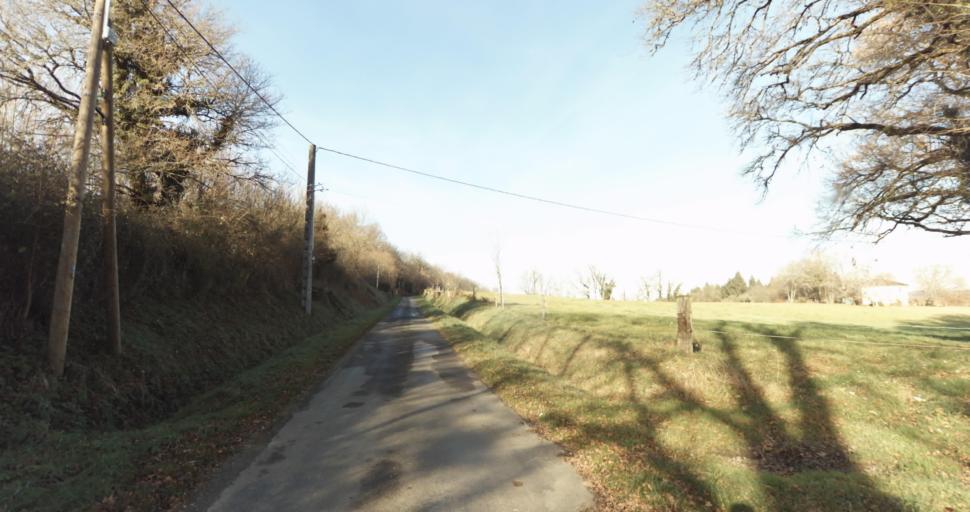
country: FR
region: Limousin
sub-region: Departement de la Haute-Vienne
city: Aixe-sur-Vienne
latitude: 45.7832
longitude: 1.1290
